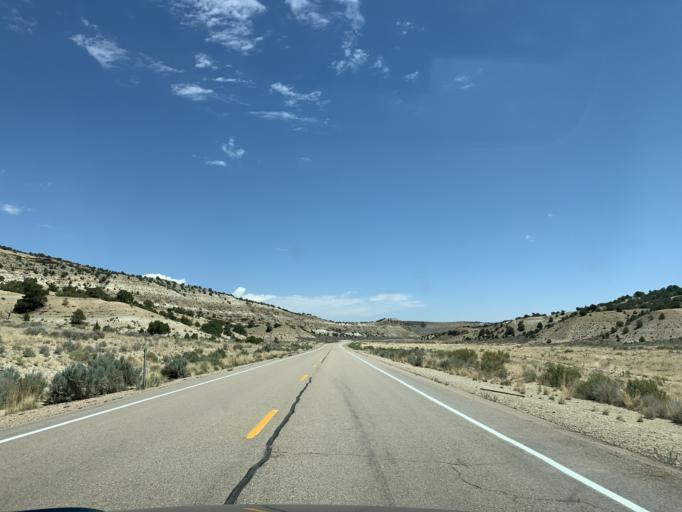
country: US
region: Utah
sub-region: Duchesne County
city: Duchesne
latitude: 39.9645
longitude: -110.1823
